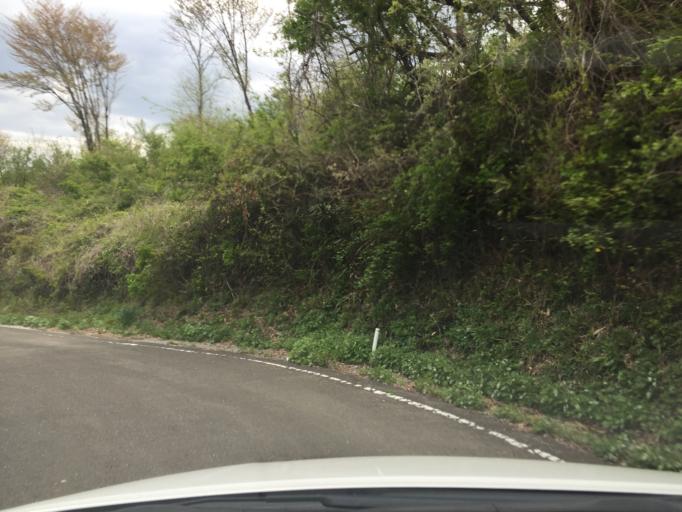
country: JP
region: Fukushima
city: Hobaramachi
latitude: 37.7058
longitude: 140.6572
